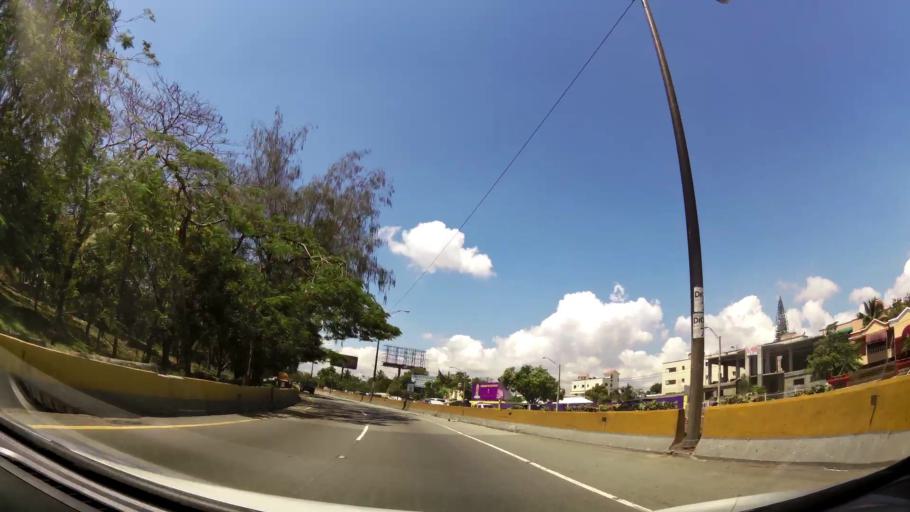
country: DO
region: Santo Domingo
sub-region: Santo Domingo
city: Santo Domingo Este
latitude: 18.4854
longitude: -69.8493
